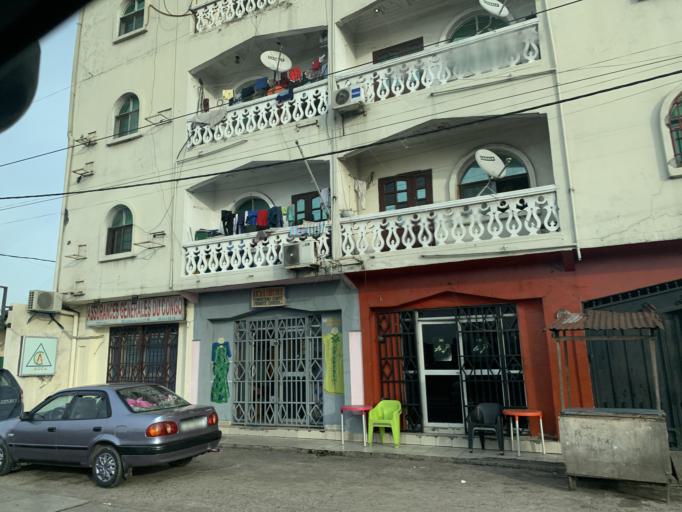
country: CG
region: Brazzaville
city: Brazzaville
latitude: -4.2484
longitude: 15.2809
